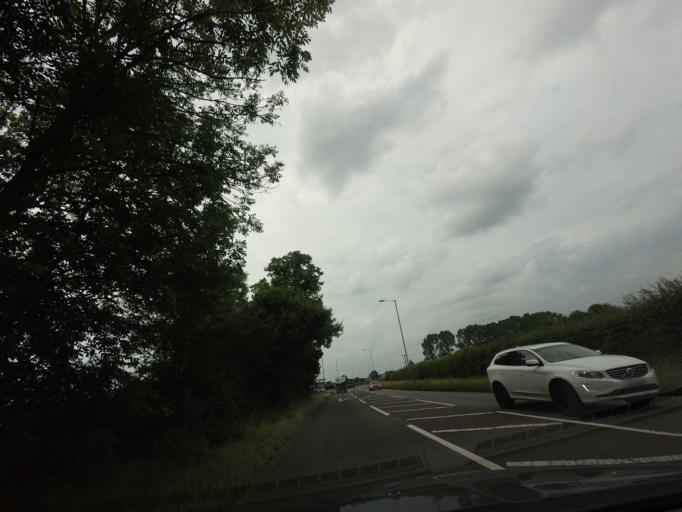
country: GB
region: England
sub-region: Shropshire
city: Tong
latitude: 52.6692
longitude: -2.3088
